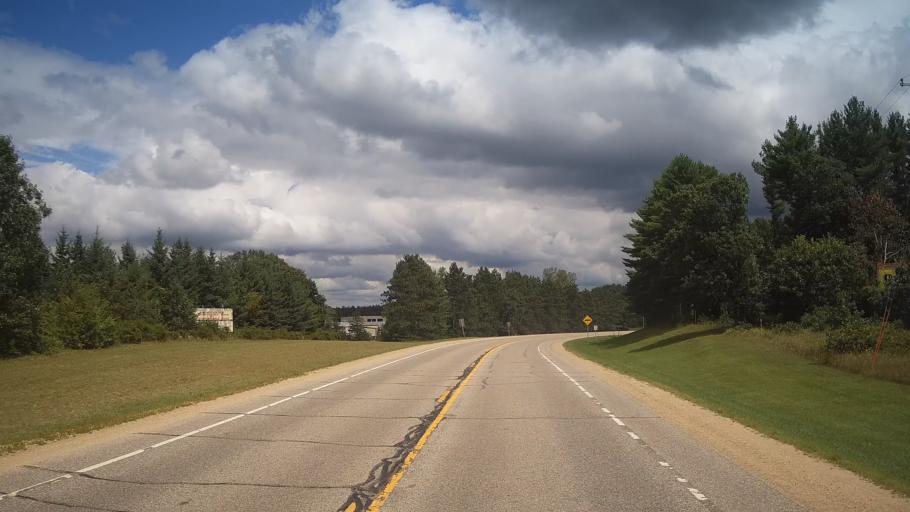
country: US
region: Wisconsin
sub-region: Marquette County
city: Westfield
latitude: 44.0380
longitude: -89.5129
